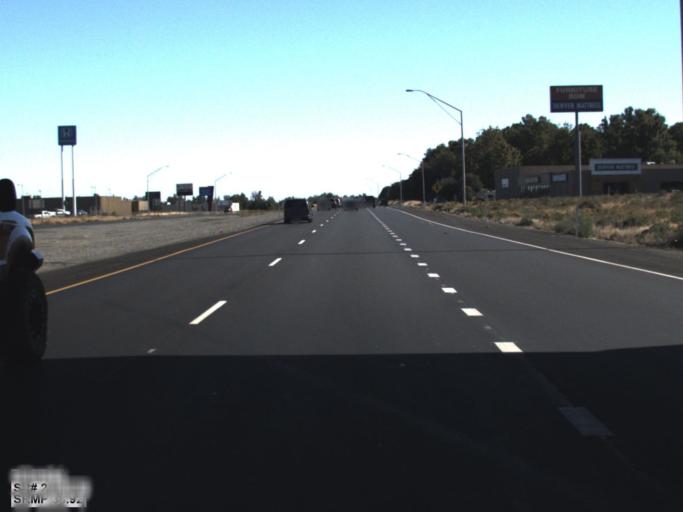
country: US
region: Washington
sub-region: Franklin County
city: West Pasco
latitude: 46.2324
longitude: -119.2231
